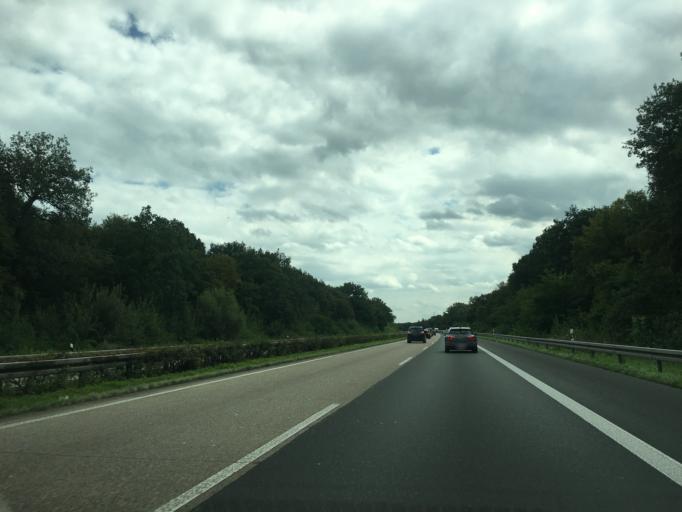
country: DE
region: North Rhine-Westphalia
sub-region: Regierungsbezirk Munster
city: Ascheberg
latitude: 51.8499
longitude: 7.5802
